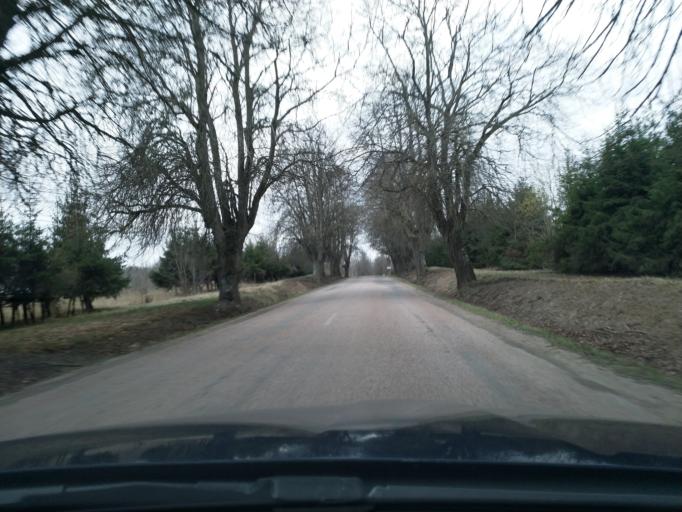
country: LV
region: Talsu Rajons
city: Sabile
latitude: 56.9280
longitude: 22.5648
